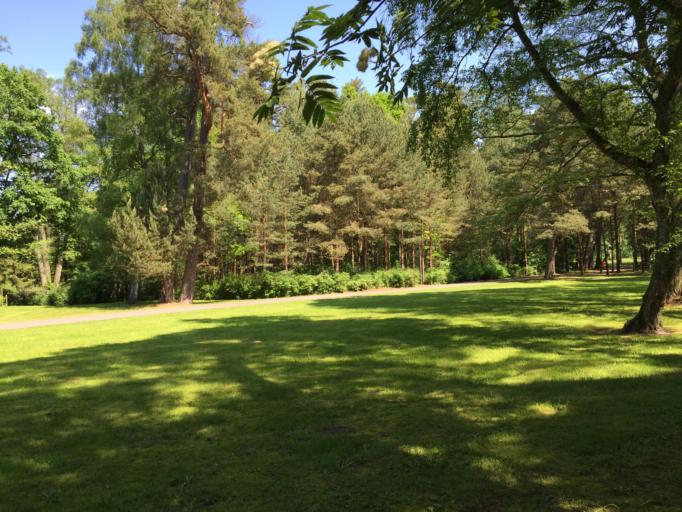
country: LT
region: Klaipedos apskritis
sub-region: Klaipeda
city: Palanga
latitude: 55.9036
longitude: 21.0601
